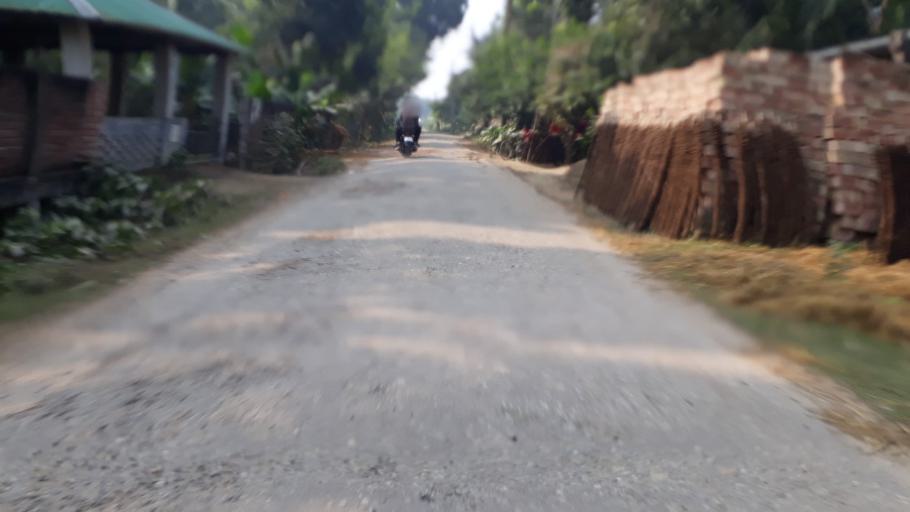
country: BD
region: Khulna
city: Kaliganj
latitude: 23.3509
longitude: 88.8967
